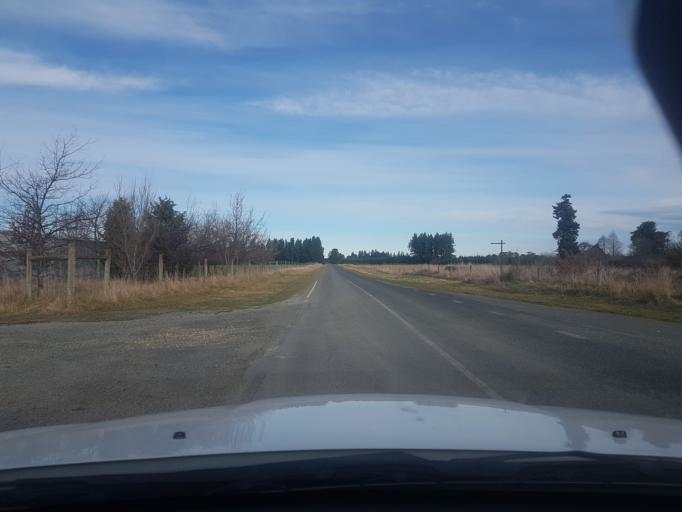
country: NZ
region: Canterbury
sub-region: Timaru District
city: Pleasant Point
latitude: -43.9364
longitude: 171.2624
